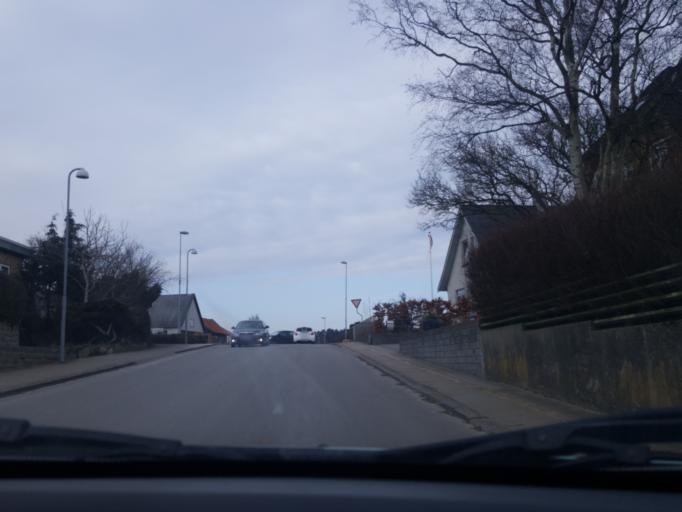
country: DK
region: Zealand
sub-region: Kalundborg Kommune
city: Kalundborg
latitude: 55.6842
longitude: 11.0680
